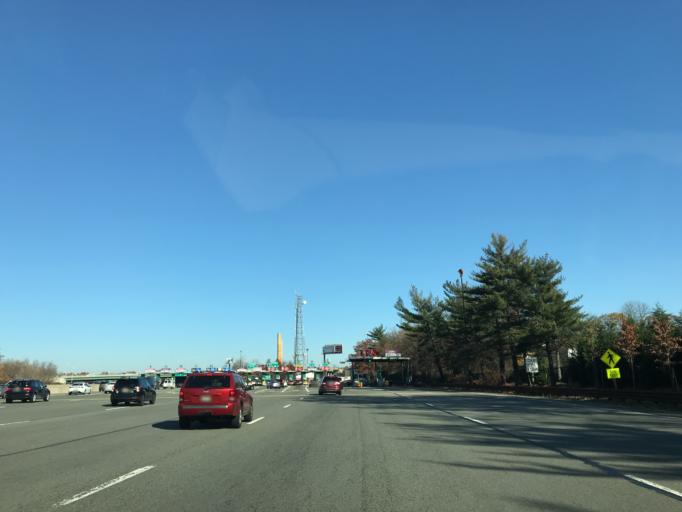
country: US
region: New Jersey
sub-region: Union County
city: Union
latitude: 40.7018
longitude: -74.2480
